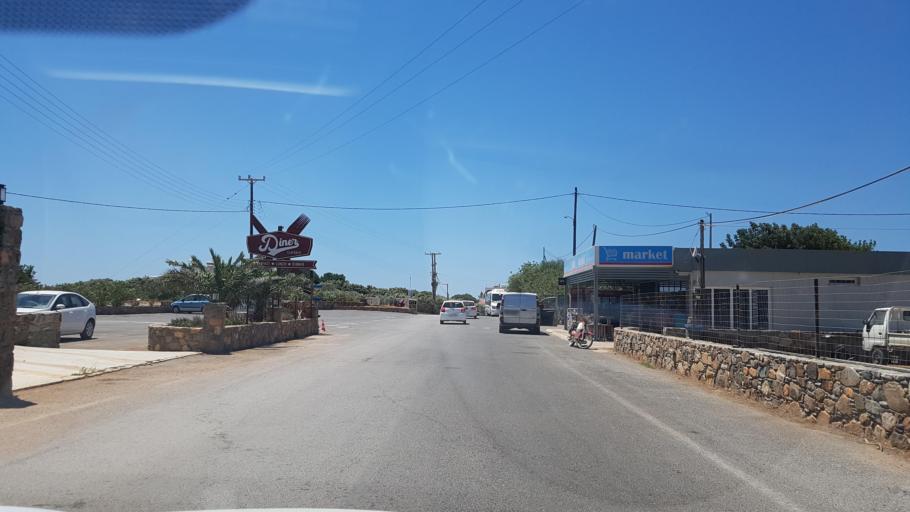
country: GR
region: Crete
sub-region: Nomos Chanias
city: Palaiochora
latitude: 35.2782
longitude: 23.5457
